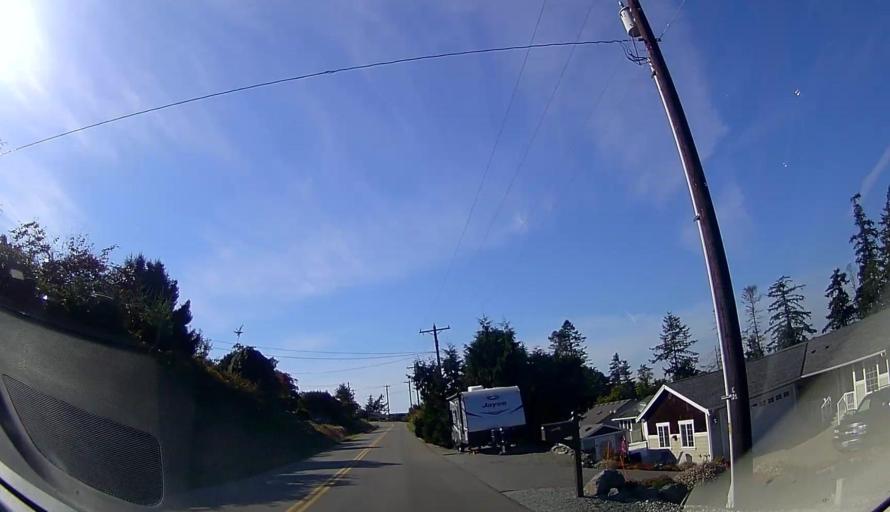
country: US
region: Washington
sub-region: Island County
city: Camano
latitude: 48.2454
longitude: -122.5289
